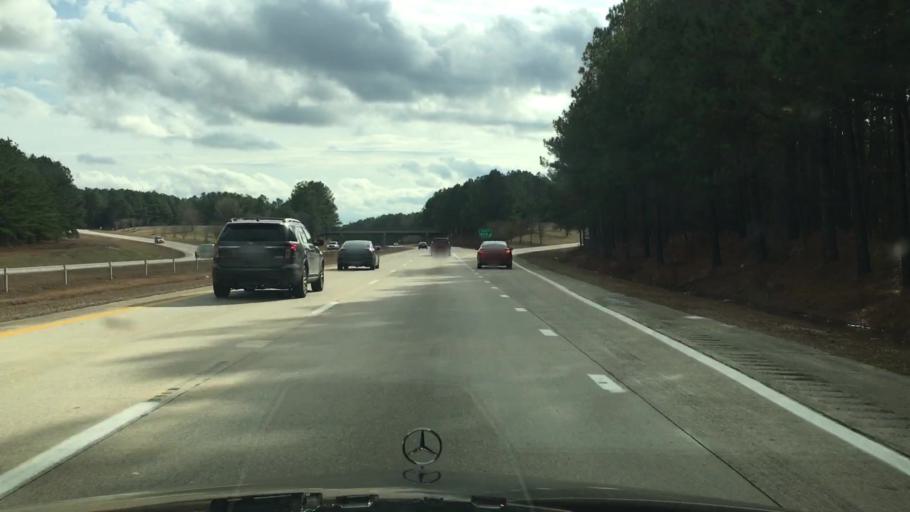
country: US
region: North Carolina
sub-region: Johnston County
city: Benson
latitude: 35.4264
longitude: -78.5313
